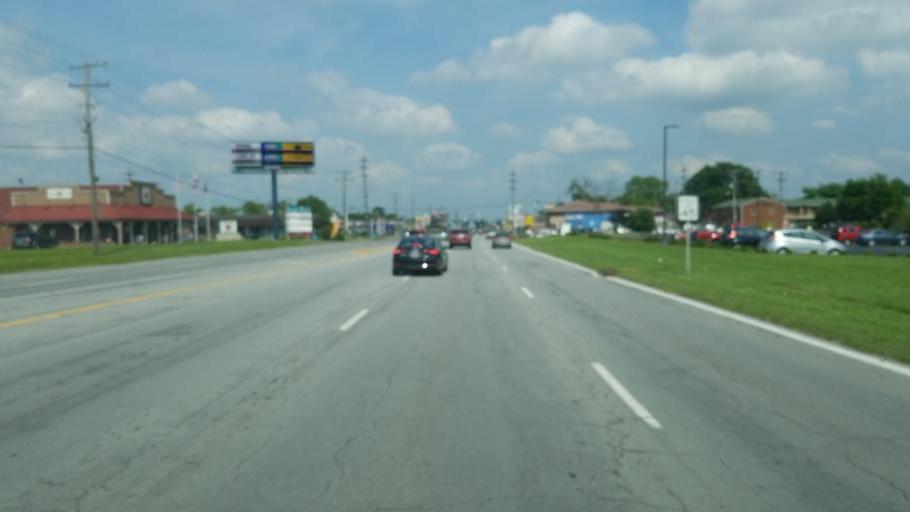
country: US
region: Ohio
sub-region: Franklin County
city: Lincoln Village
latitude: 39.9535
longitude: -83.1026
